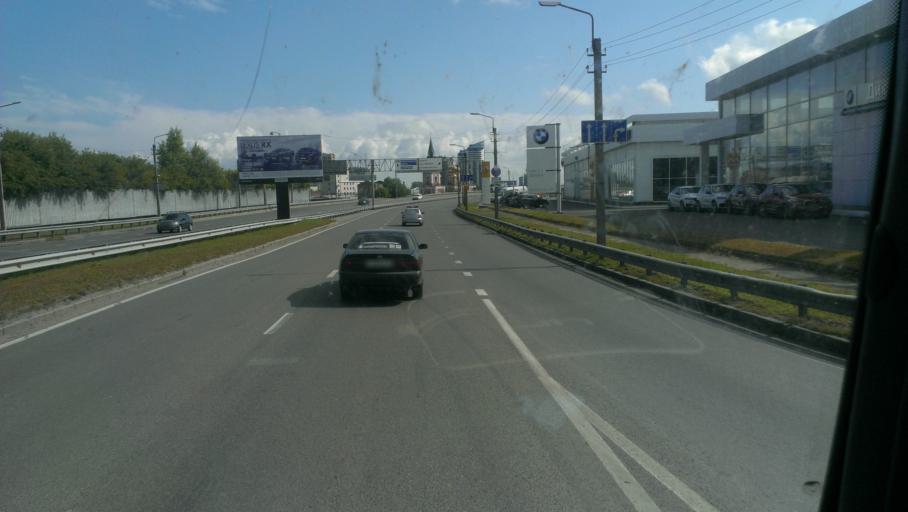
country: RU
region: Altai Krai
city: Zaton
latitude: 53.3250
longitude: 83.7910
